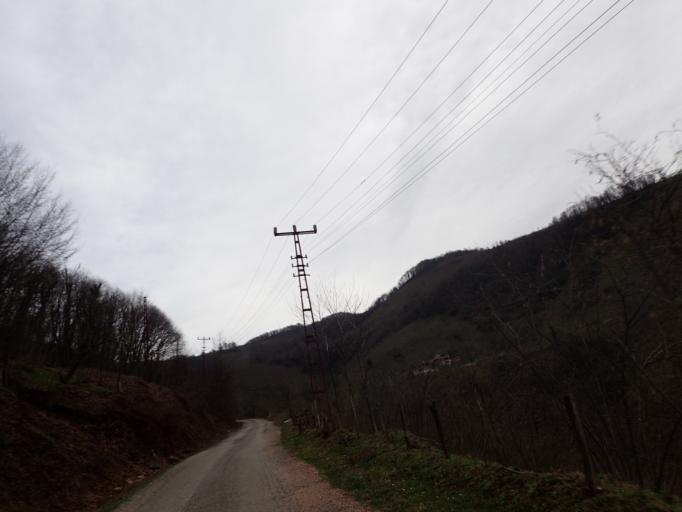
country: TR
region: Ordu
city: Camas
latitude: 40.8844
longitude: 37.5164
